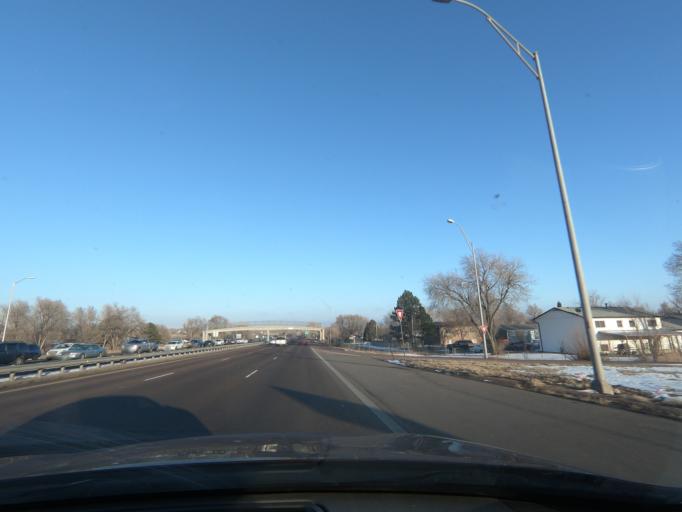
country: US
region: Colorado
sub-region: El Paso County
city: Stratmoor
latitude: 38.7646
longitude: -104.7718
